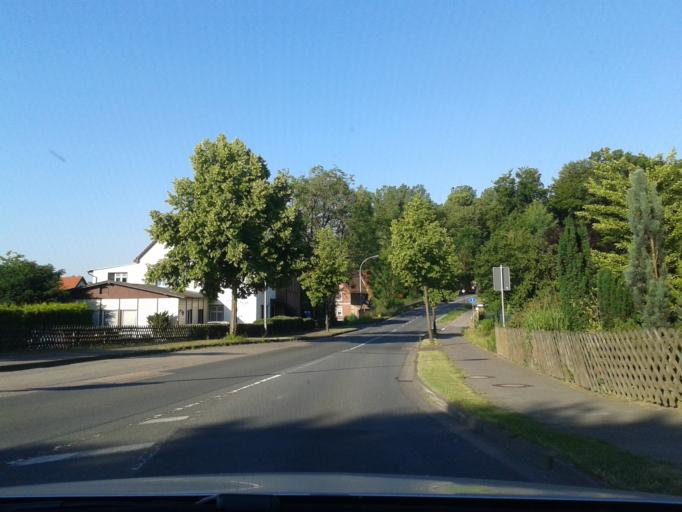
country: DE
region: North Rhine-Westphalia
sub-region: Regierungsbezirk Detmold
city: Dorentrup
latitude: 52.0333
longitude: 8.9843
